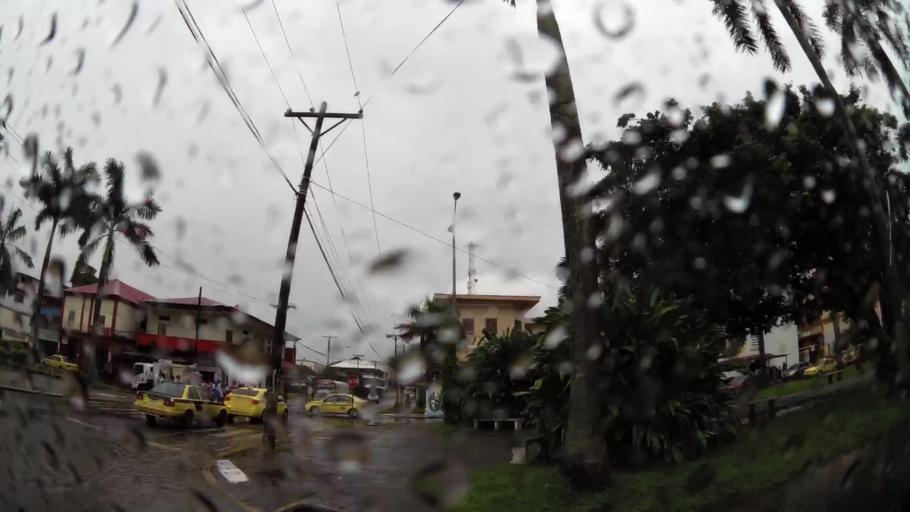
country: PA
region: Colon
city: Colon
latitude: 9.3646
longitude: -79.9035
